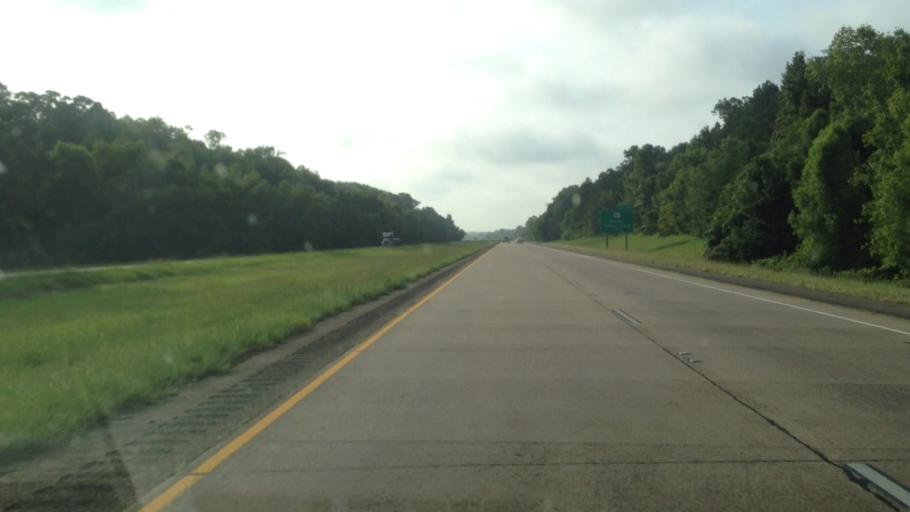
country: US
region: Louisiana
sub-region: Rapides Parish
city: Lecompte
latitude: 31.0237
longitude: -92.3966
